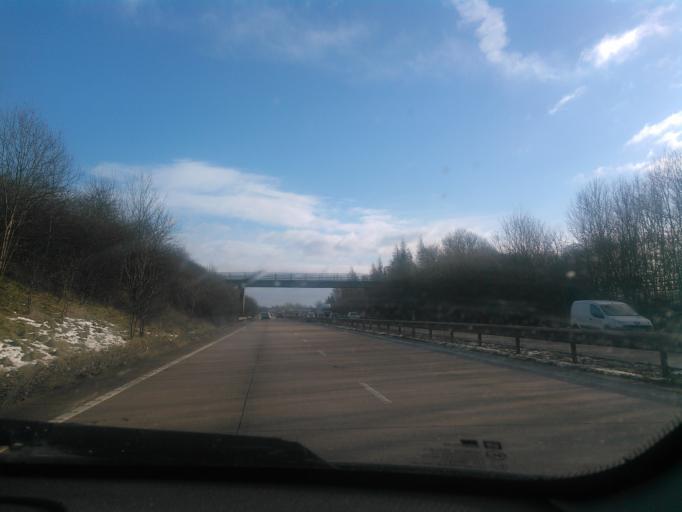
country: GB
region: England
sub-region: Staffordshire
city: Cheadle
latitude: 52.9397
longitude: -1.9922
